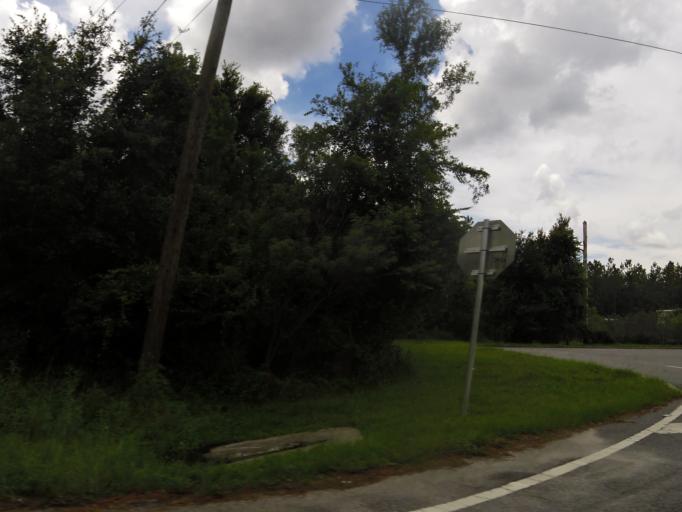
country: US
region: Florida
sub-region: Saint Johns County
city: Saint Augustine Shores
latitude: 29.6638
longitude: -81.4137
